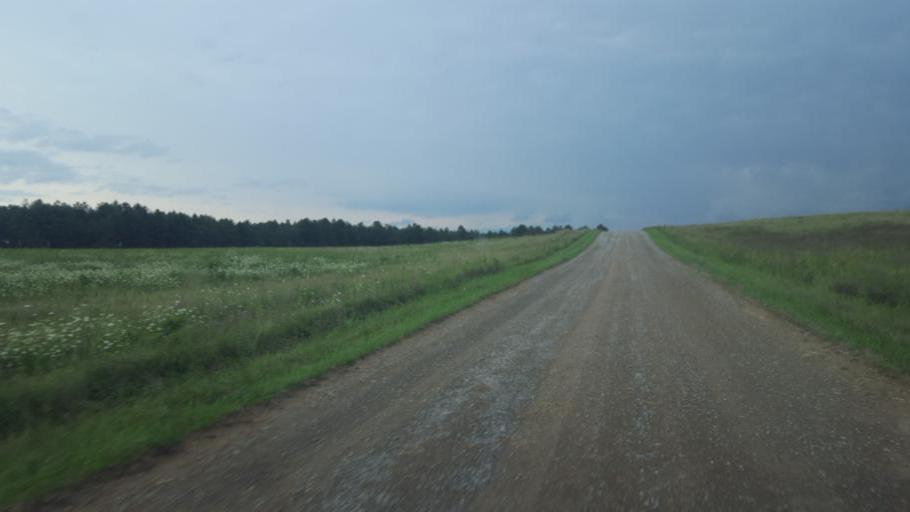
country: US
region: Pennsylvania
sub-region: Clarion County
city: Knox
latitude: 41.1458
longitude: -79.5026
